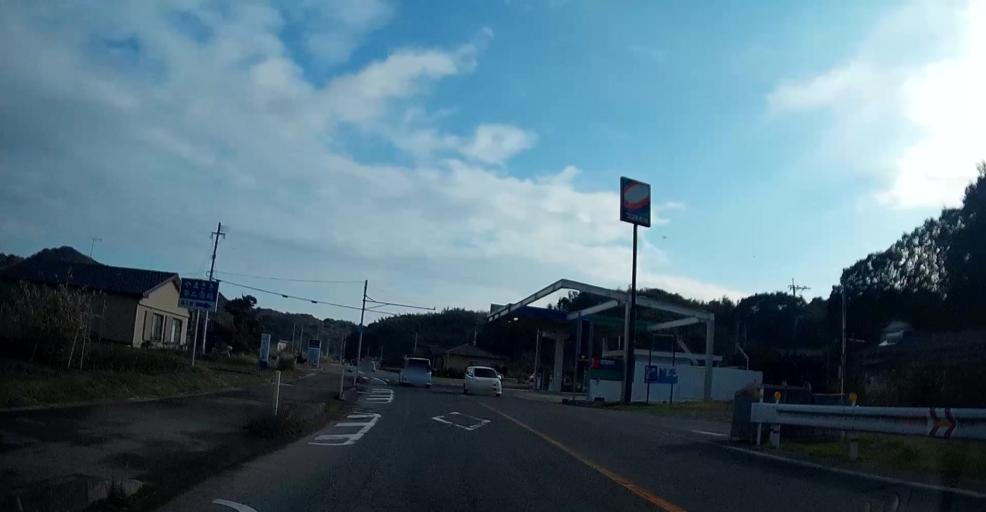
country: JP
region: Kumamoto
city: Yatsushiro
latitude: 32.5648
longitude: 130.4099
